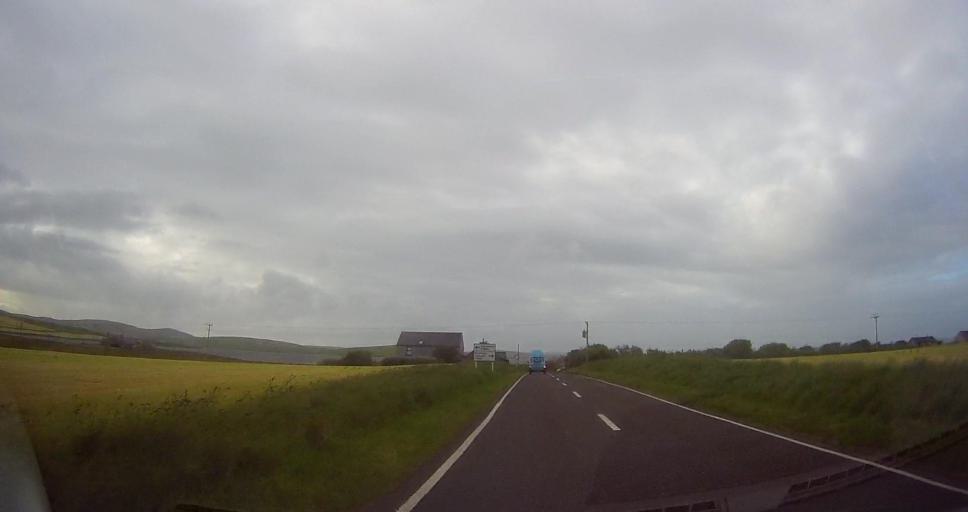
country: GB
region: Scotland
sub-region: Orkney Islands
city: Stromness
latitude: 58.9818
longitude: -3.2461
